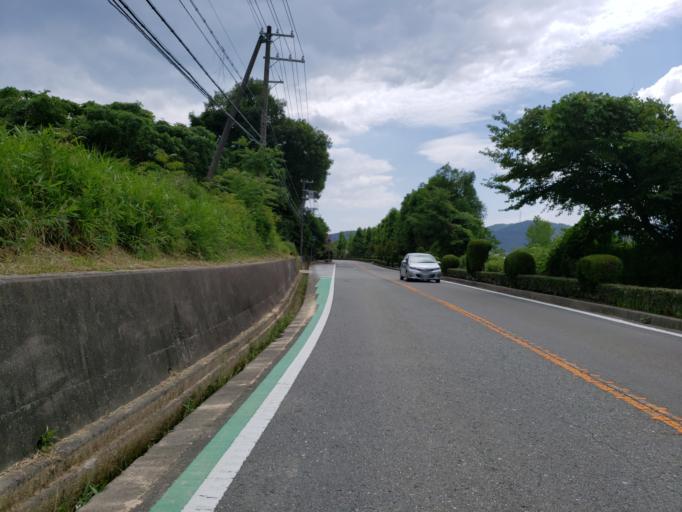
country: JP
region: Hyogo
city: Aioi
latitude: 34.7848
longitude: 134.4766
